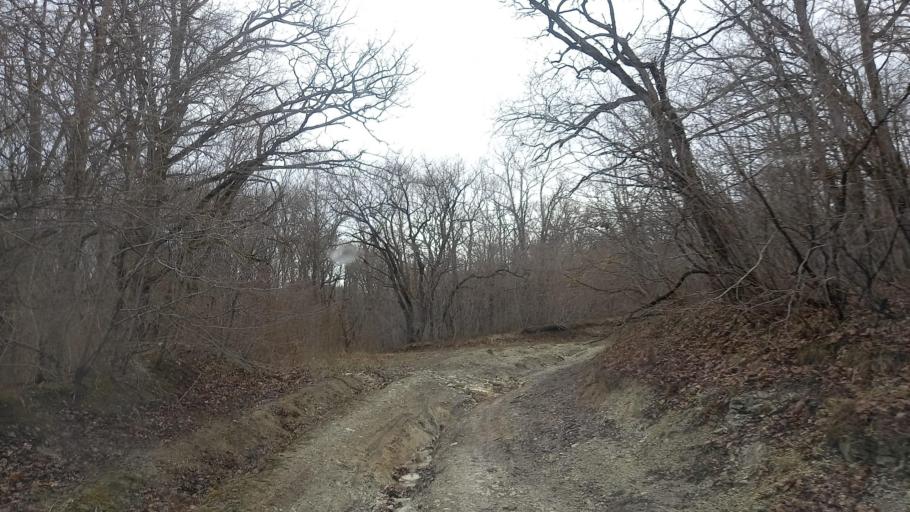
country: RU
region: Krasnodarskiy
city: Novorossiysk
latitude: 44.8567
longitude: 37.8426
